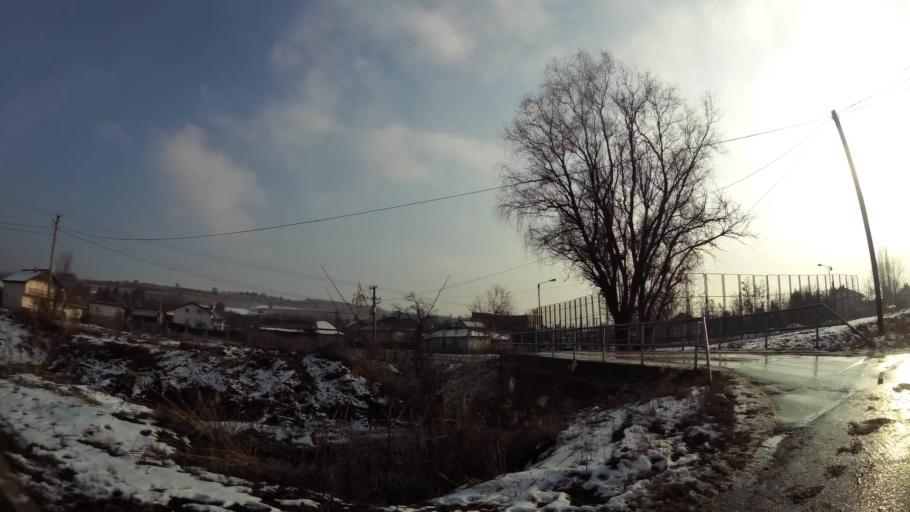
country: MK
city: Miladinovci
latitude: 41.9797
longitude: 21.6496
